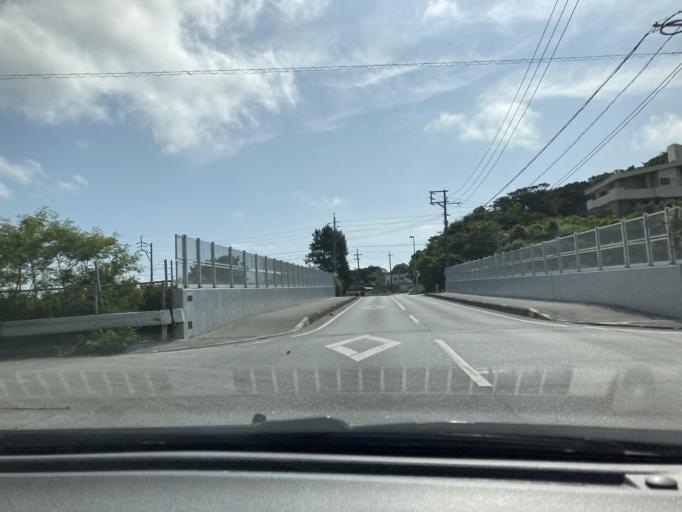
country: JP
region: Okinawa
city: Chatan
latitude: 26.2960
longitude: 127.7912
